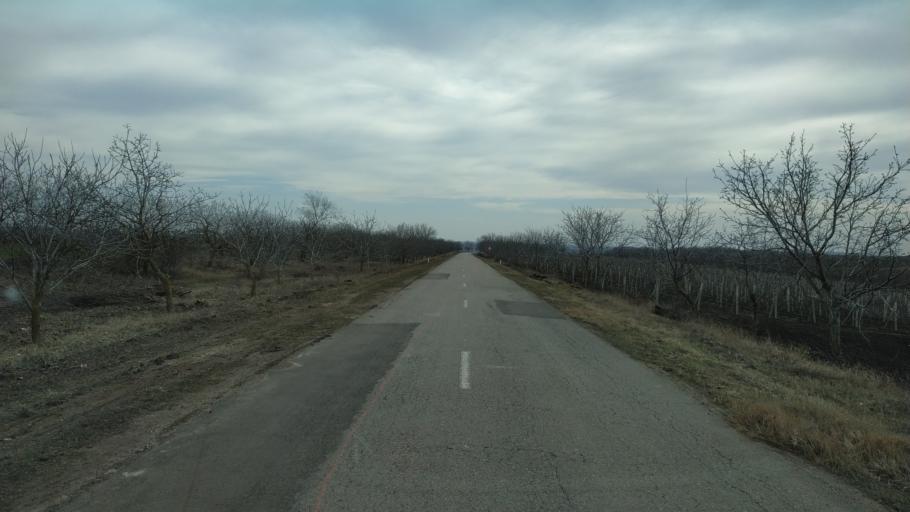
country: MD
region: Nisporeni
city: Nisporeni
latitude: 46.9490
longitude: 28.2401
